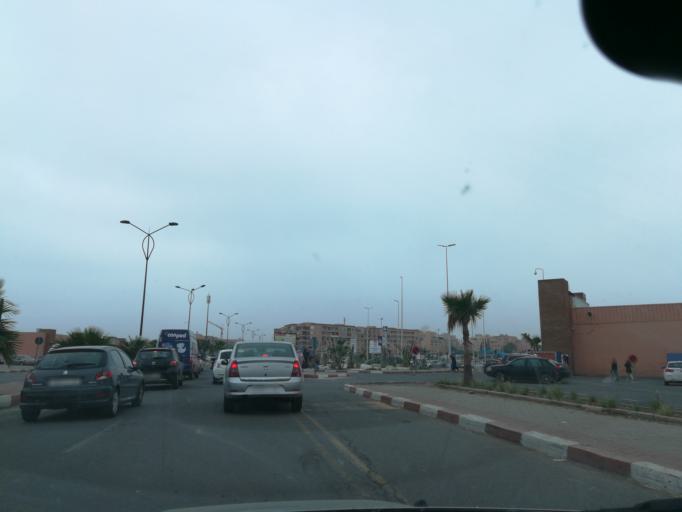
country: MA
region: Marrakech-Tensift-Al Haouz
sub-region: Marrakech
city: Marrakesh
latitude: 31.6694
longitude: -8.0125
